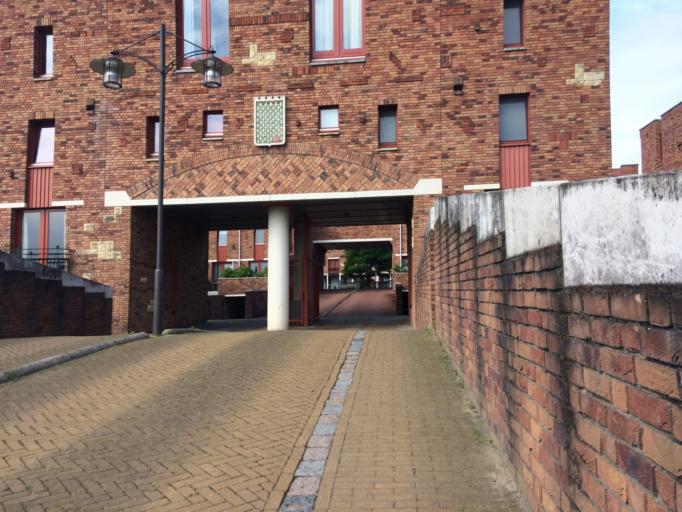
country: NL
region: Gelderland
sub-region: Gemeente Maasdriel
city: Hedel
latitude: 51.7289
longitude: 5.2486
